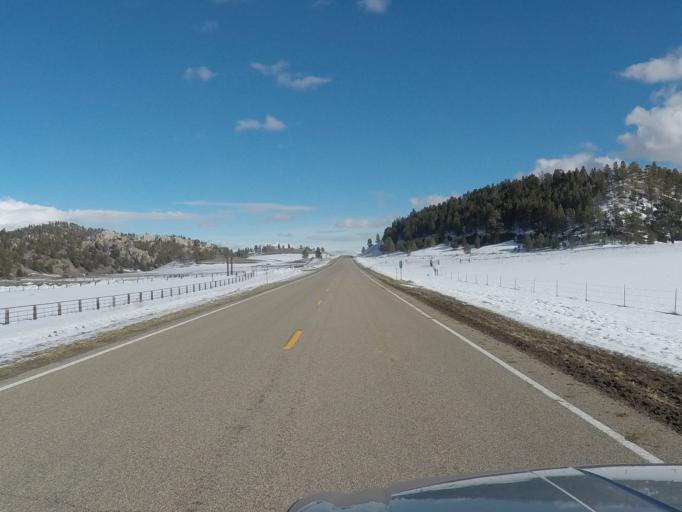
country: US
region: Montana
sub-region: Meagher County
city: White Sulphur Springs
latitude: 46.5484
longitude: -110.4703
